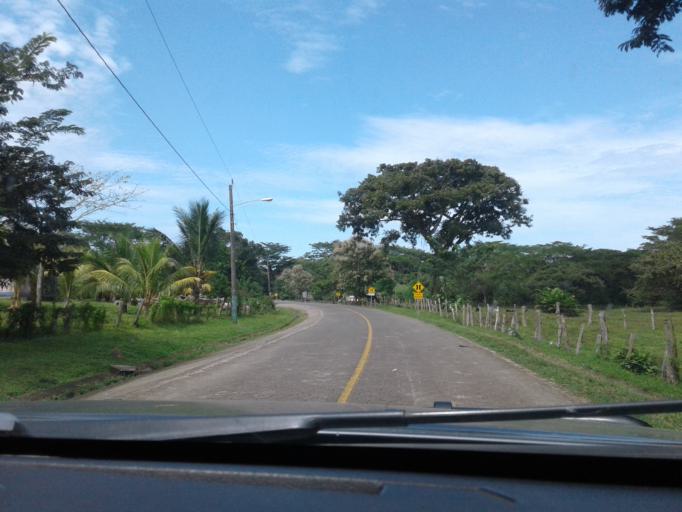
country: NI
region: Rivas
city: Cardenas
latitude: 11.1823
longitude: -85.4899
